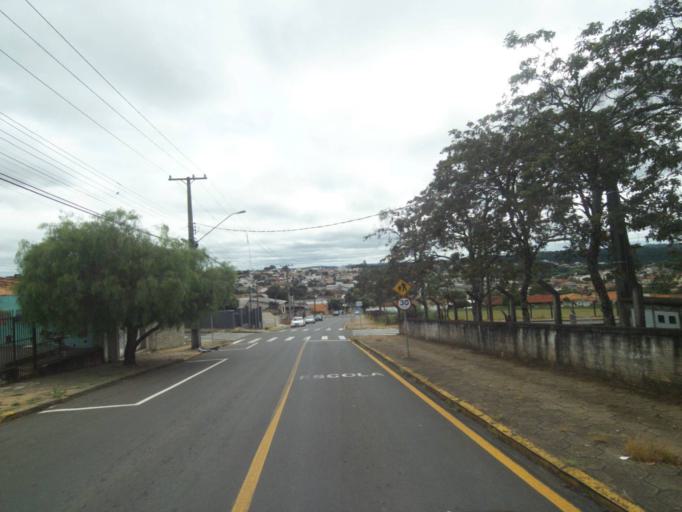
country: BR
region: Parana
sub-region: Telemaco Borba
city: Telemaco Borba
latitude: -24.3383
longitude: -50.6234
